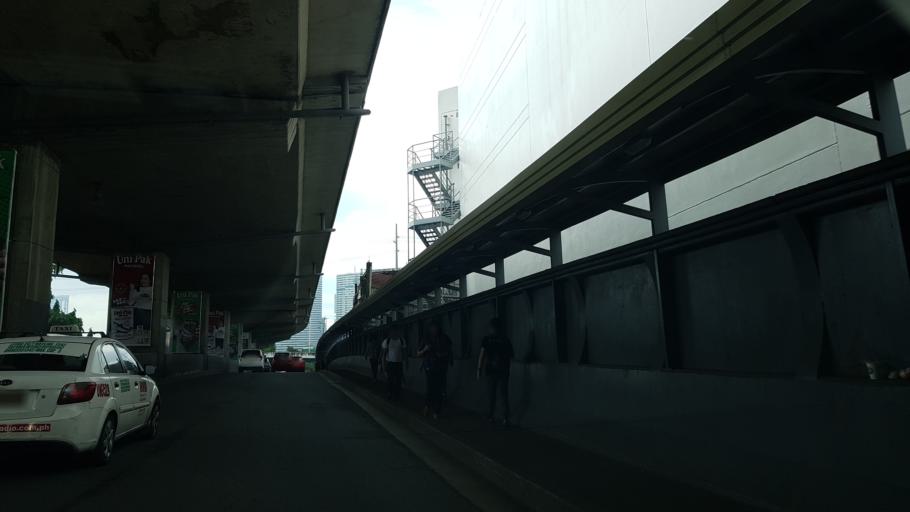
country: PH
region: Metro Manila
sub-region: Makati City
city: Makati City
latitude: 14.5562
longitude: 121.0430
